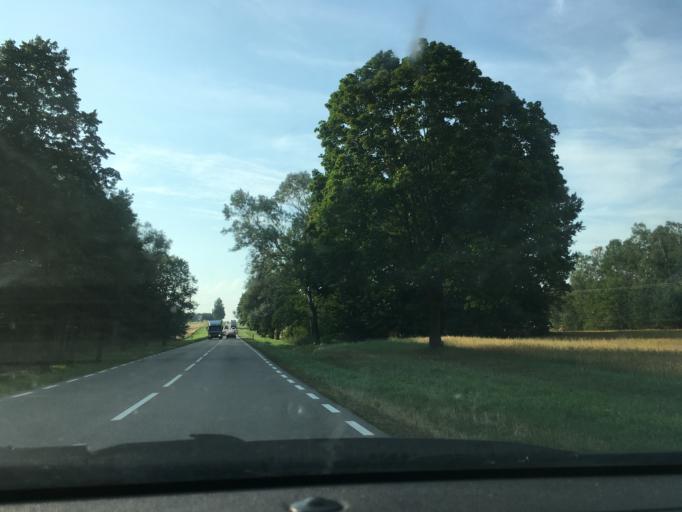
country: PL
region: Podlasie
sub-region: Powiat moniecki
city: Knyszyn
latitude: 53.2839
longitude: 22.9480
